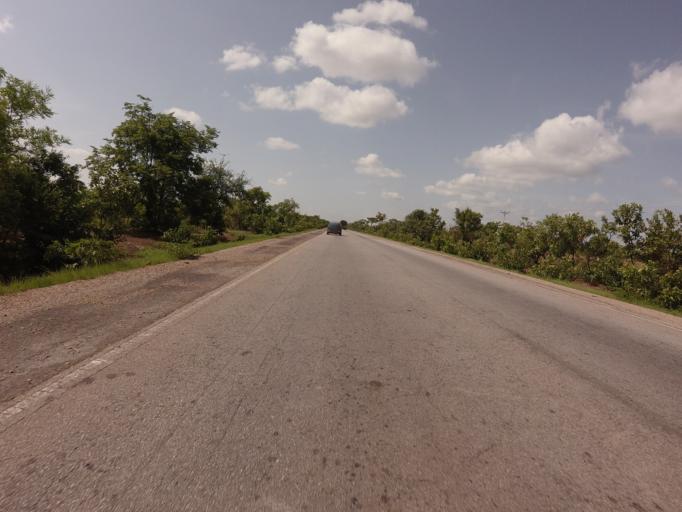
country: GH
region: Northern
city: Savelugu
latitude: 9.9520
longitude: -0.8361
